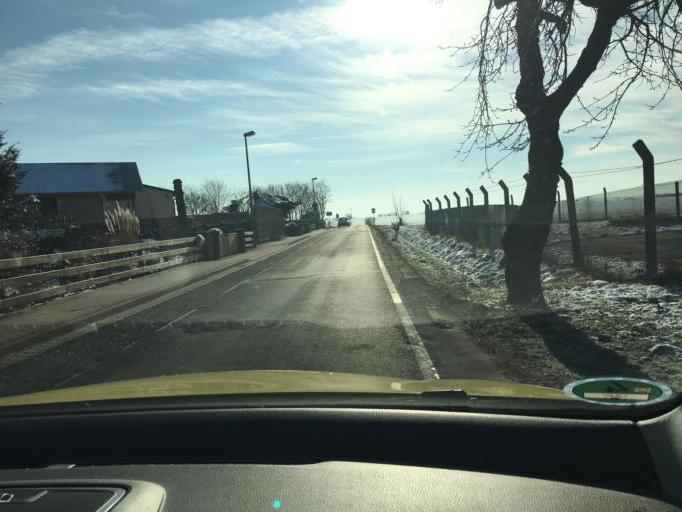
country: DE
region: Saxony
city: Belgershain
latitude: 51.2539
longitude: 12.5397
